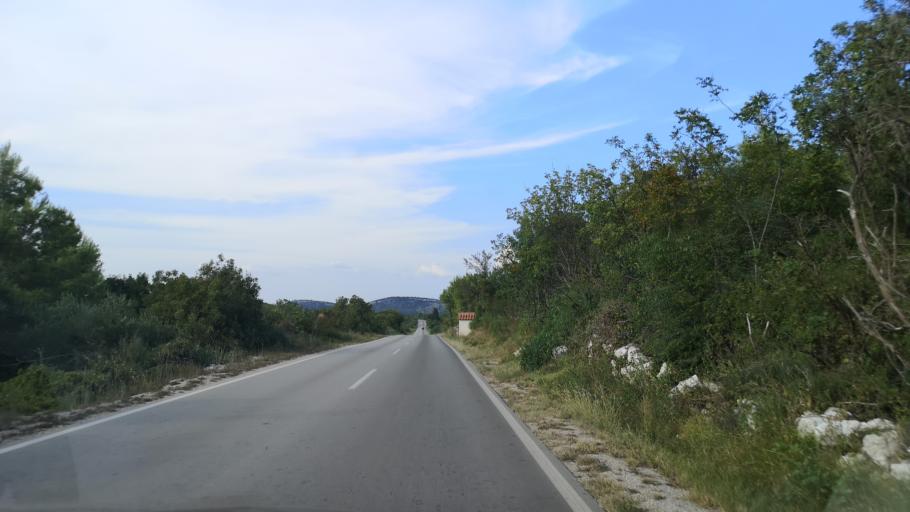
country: HR
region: Sibensko-Kniniska
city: Vodice
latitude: 43.8040
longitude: 15.7741
